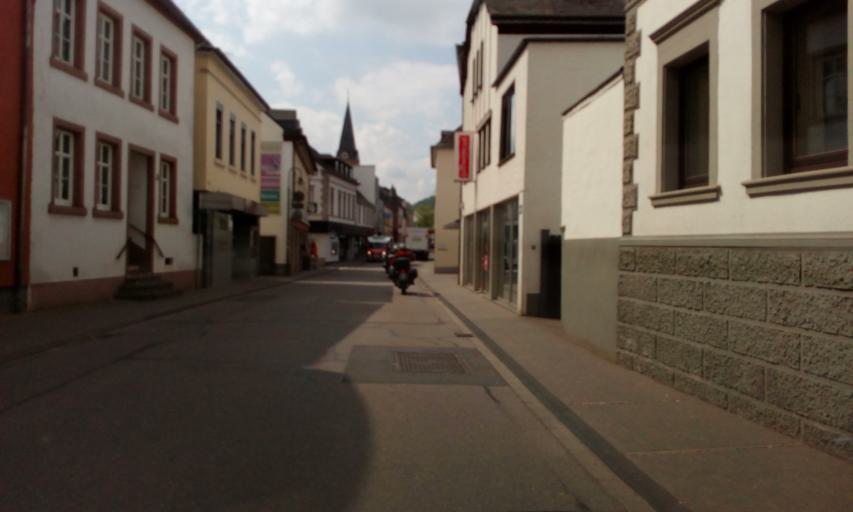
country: DE
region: Rheinland-Pfalz
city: Schweich
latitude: 49.8237
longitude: 6.7533
